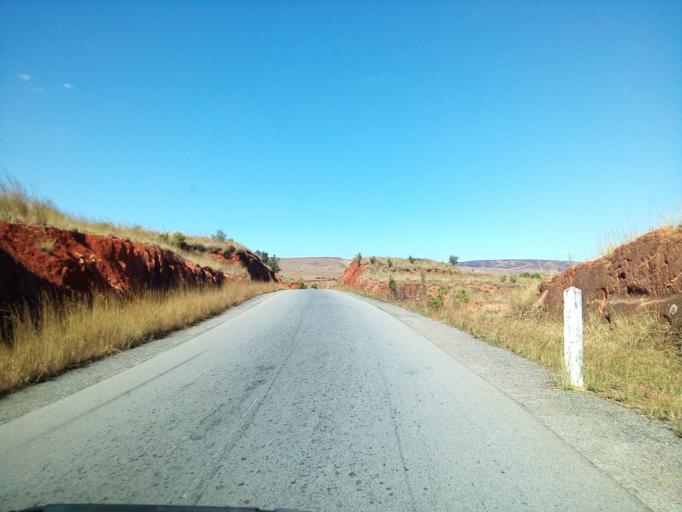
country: MG
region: Betsiboka
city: Maevatanana
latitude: -17.4197
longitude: 46.9304
